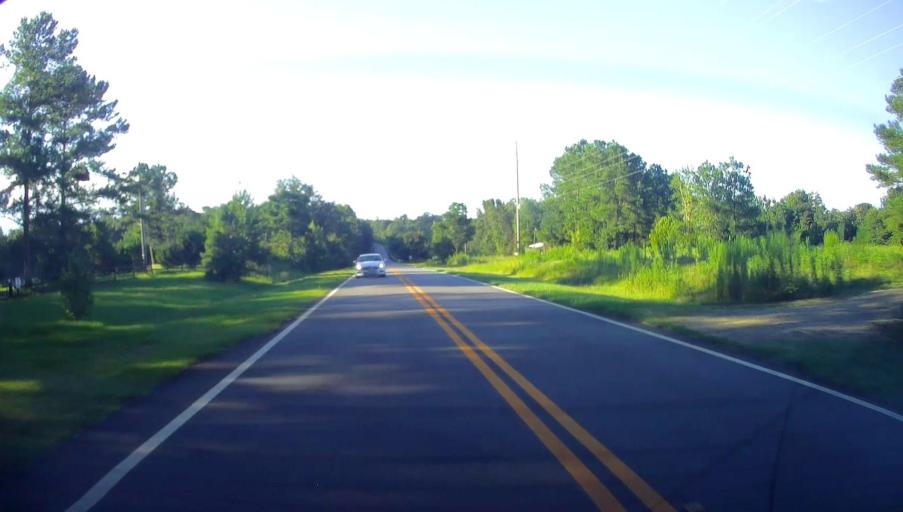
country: US
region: Georgia
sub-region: Pulaski County
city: Hawkinsville
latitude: 32.2975
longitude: -83.4498
